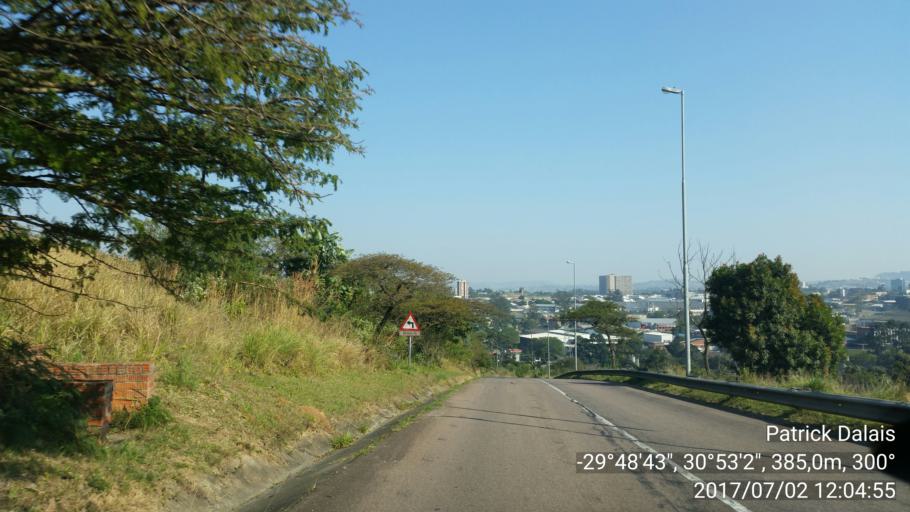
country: ZA
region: KwaZulu-Natal
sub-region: eThekwini Metropolitan Municipality
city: Berea
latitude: -29.8120
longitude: 30.8843
